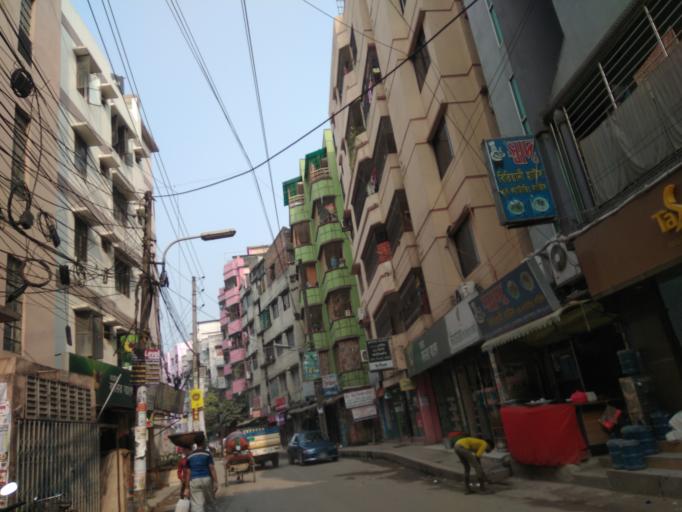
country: BD
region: Dhaka
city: Azimpur
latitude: 23.7665
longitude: 90.3579
